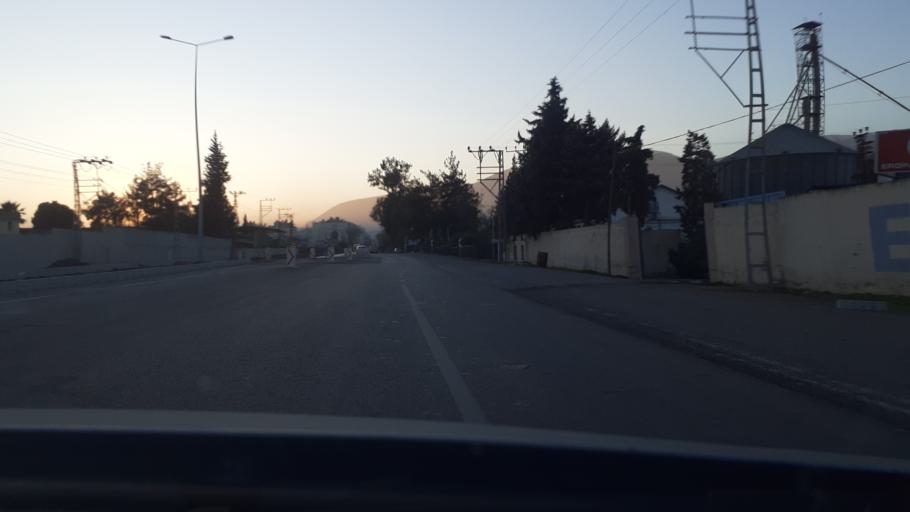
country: TR
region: Hatay
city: Kirikhan
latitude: 36.5007
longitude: 36.3782
